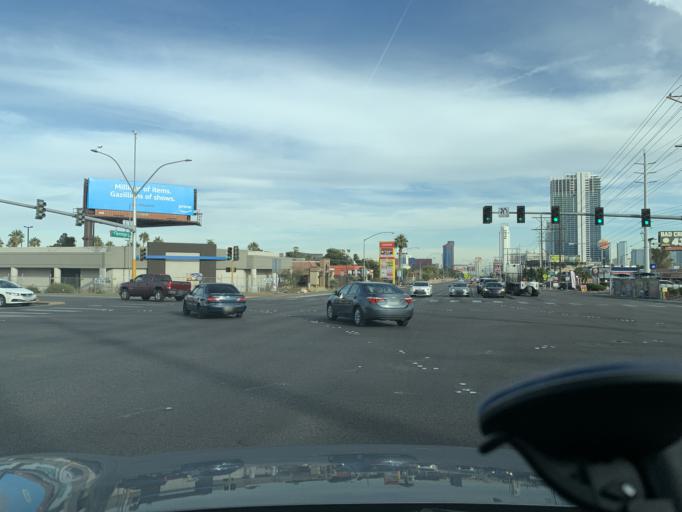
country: US
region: Nevada
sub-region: Clark County
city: Spring Valley
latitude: 36.1155
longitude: -115.2083
